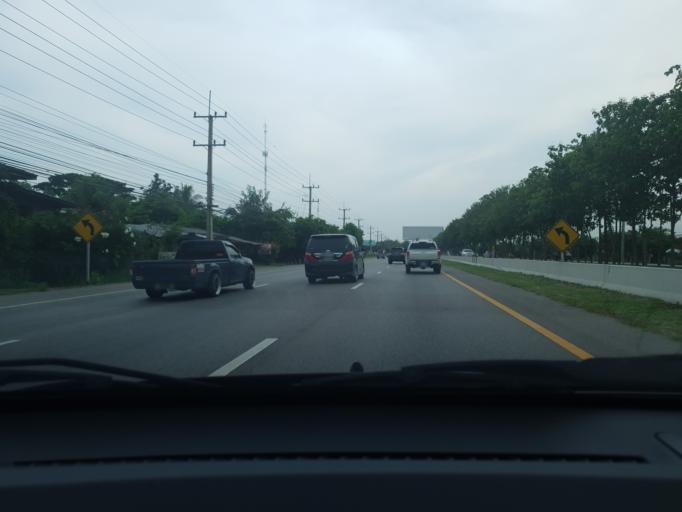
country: TH
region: Phetchaburi
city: Khao Yoi
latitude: 13.1680
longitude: 99.8412
